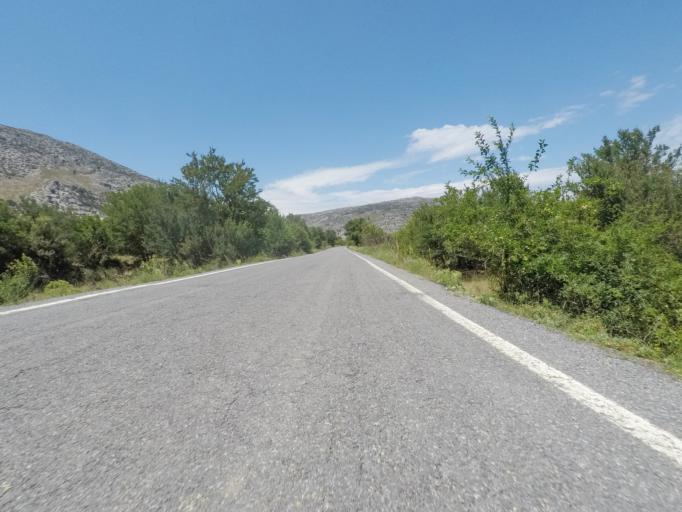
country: GR
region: Crete
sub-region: Nomos Irakleiou
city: Mokhos
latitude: 35.1796
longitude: 25.4341
